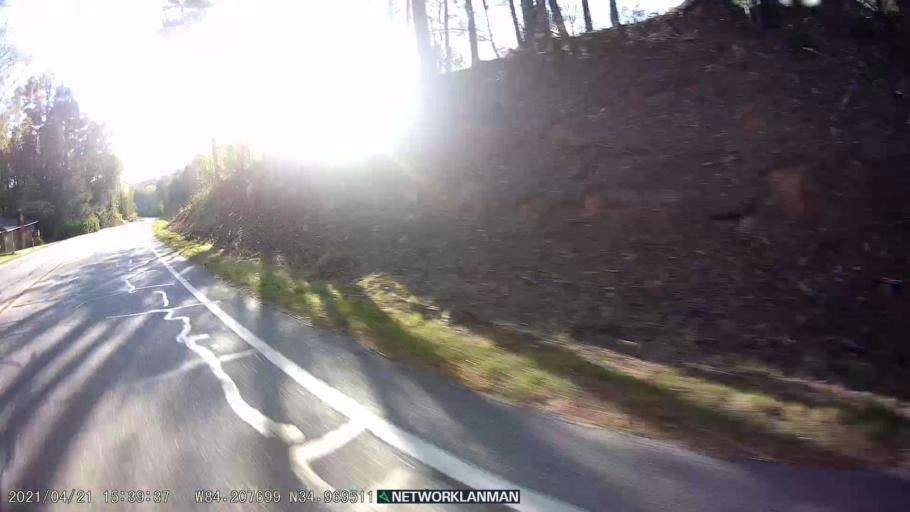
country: US
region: Georgia
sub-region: Fannin County
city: Blue Ridge
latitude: 34.9692
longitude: -84.2077
